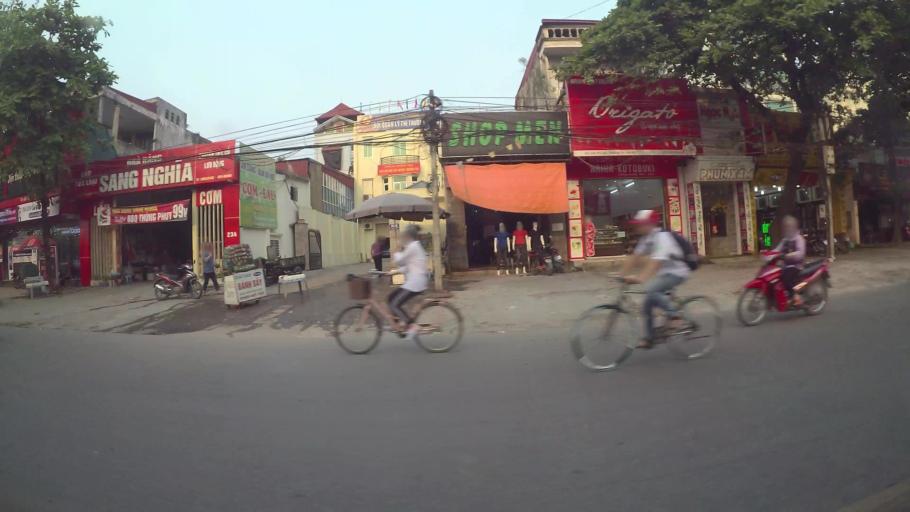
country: VN
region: Ha Noi
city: Thuong Tin
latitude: 20.8707
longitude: 105.8648
